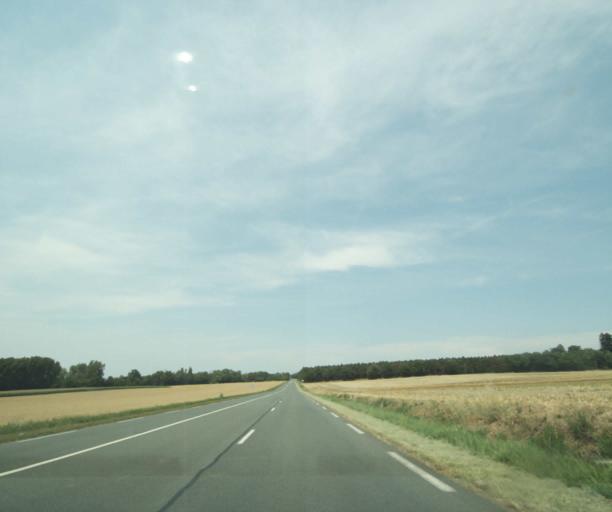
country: FR
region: Poitou-Charentes
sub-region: Departement de la Vienne
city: Vouneuil-sur-Vienne
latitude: 46.7428
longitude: 0.5542
